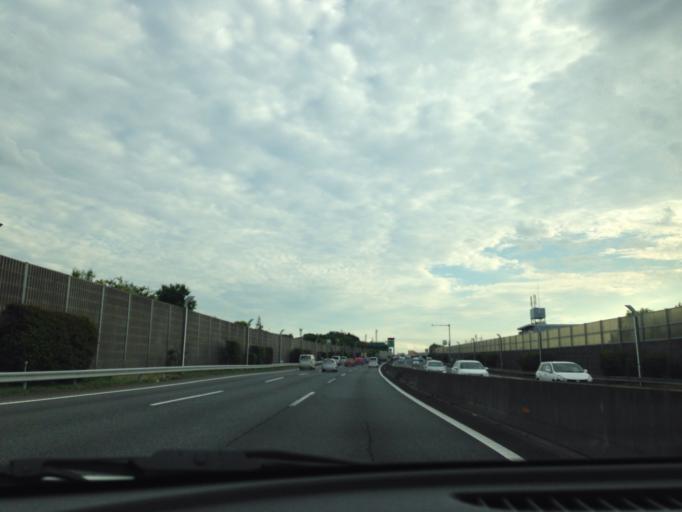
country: JP
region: Tokyo
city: Chofugaoka
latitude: 35.5997
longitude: 139.5800
